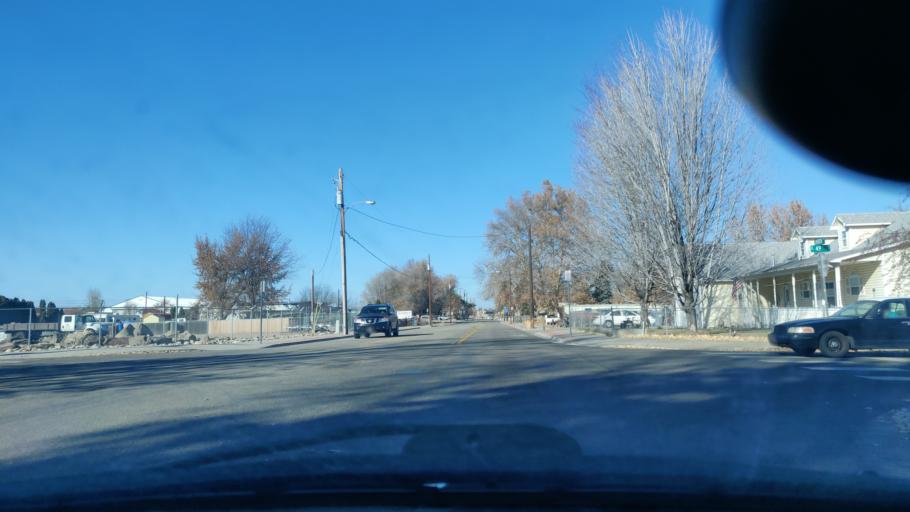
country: US
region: Idaho
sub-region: Ada County
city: Garden City
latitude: 43.6445
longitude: -116.2613
